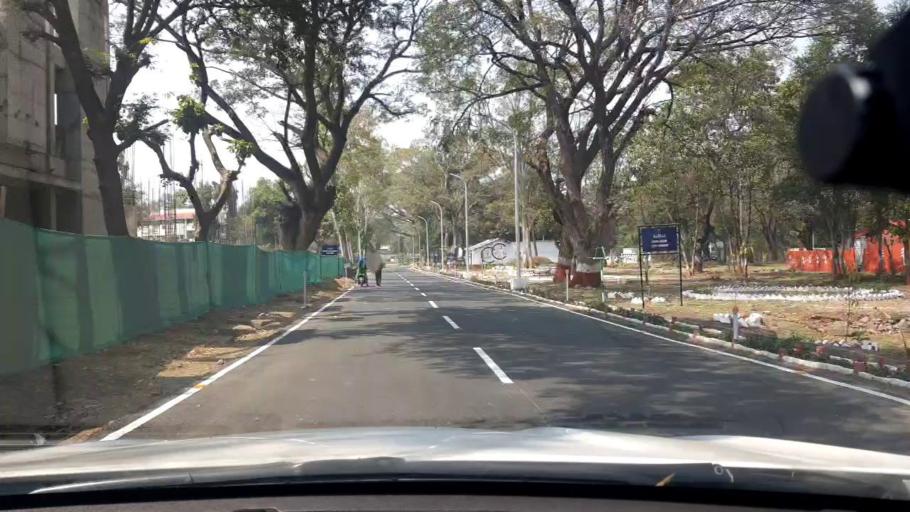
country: IN
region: Maharashtra
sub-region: Pune Division
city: Khadki
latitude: 18.5529
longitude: 73.8679
